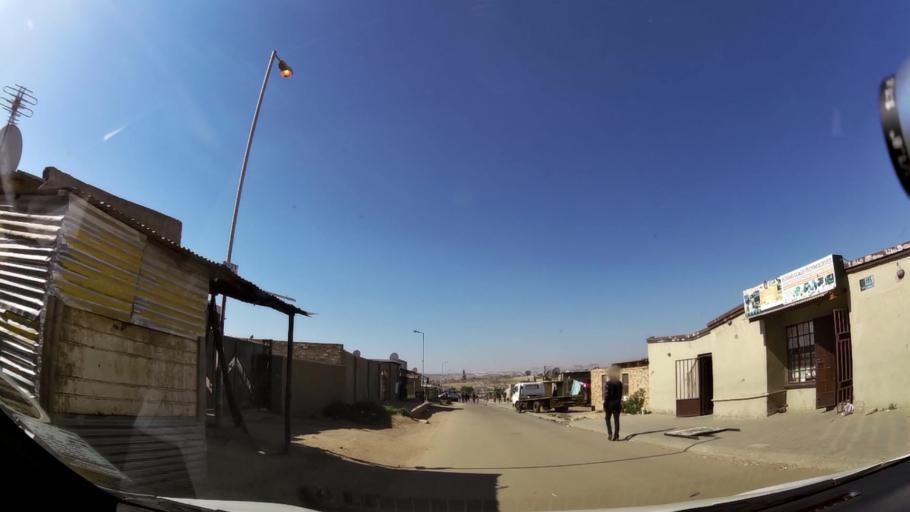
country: ZA
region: Gauteng
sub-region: City of Johannesburg Metropolitan Municipality
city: Midrand
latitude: -25.9175
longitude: 28.0919
